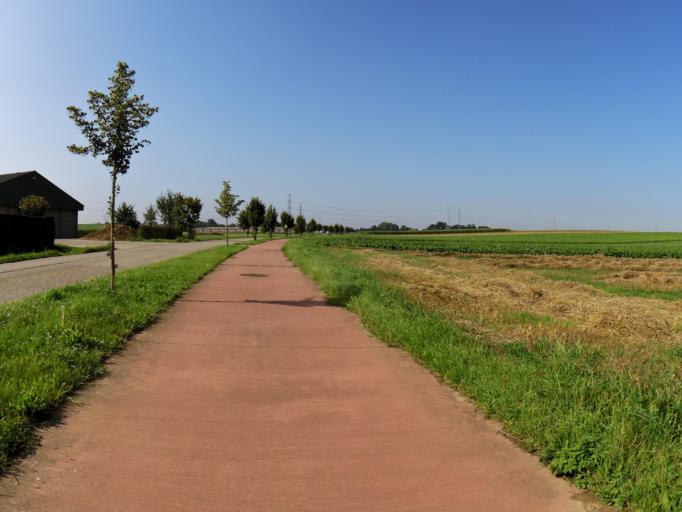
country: BE
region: Flanders
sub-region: Provincie Limburg
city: Riemst
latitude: 50.8015
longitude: 5.6018
